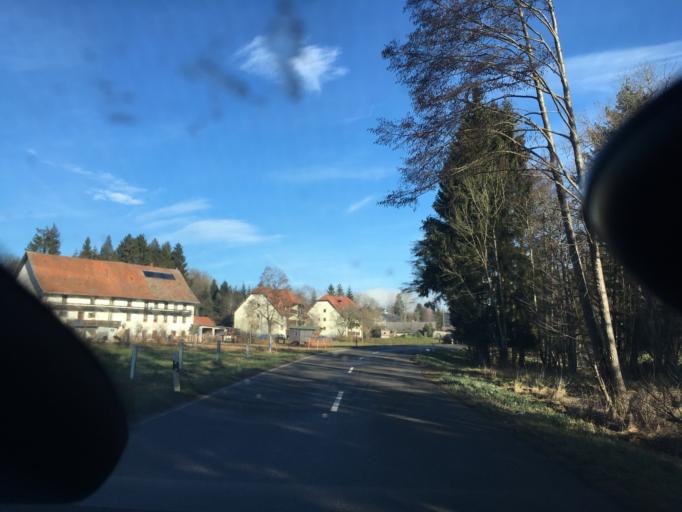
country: DE
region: Baden-Wuerttemberg
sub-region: Freiburg Region
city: Gorwihl
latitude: 47.6429
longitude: 8.1234
